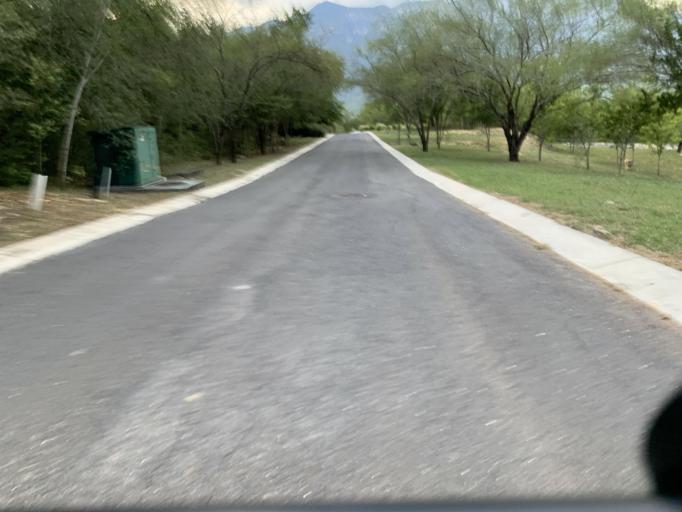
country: MX
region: Nuevo Leon
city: Santiago
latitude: 25.5090
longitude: -100.1783
